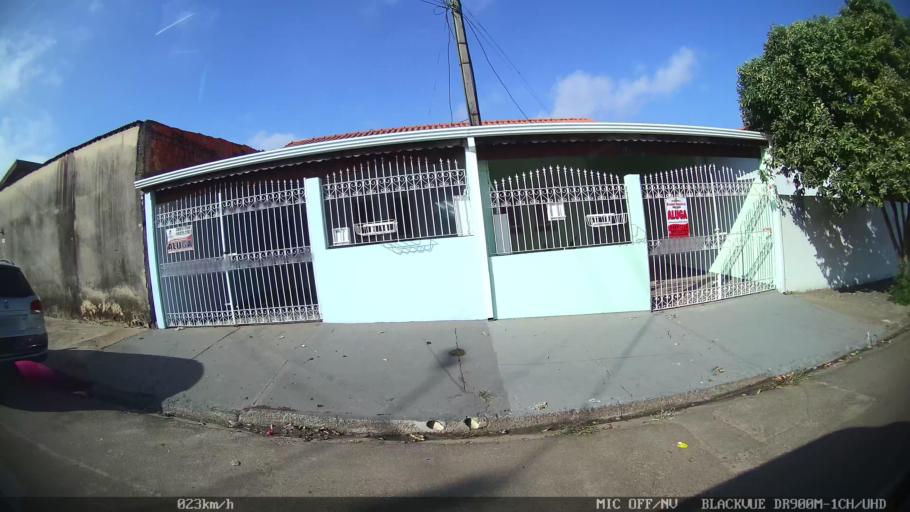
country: BR
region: Sao Paulo
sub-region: Hortolandia
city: Hortolandia
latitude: -22.9031
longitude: -47.1794
